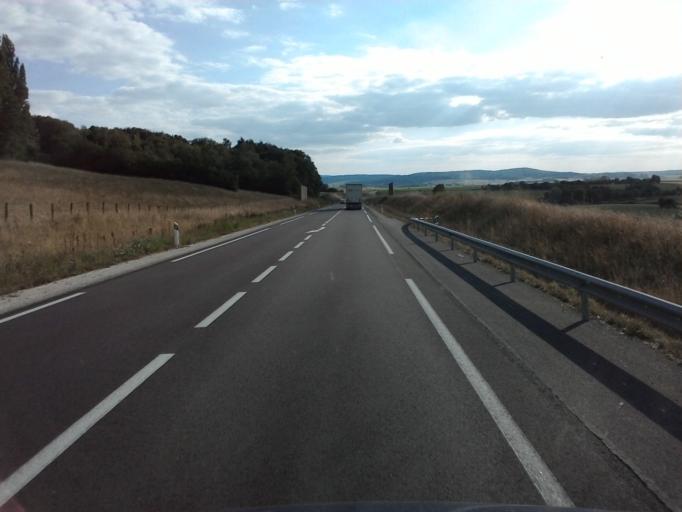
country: FR
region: Franche-Comte
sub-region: Departement de la Haute-Saone
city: Frotey-les-Vesoul
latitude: 47.7038
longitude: 6.2877
